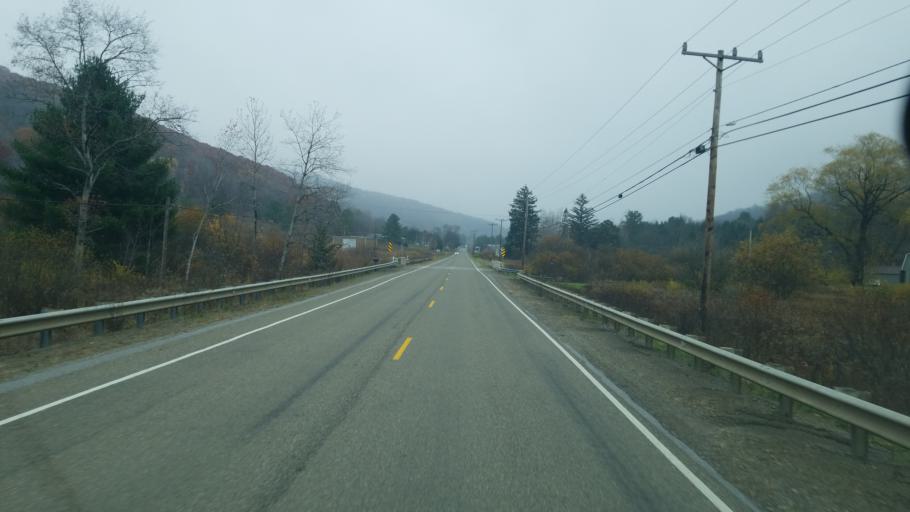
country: US
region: Pennsylvania
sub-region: McKean County
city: Smethport
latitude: 41.8793
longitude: -78.4895
